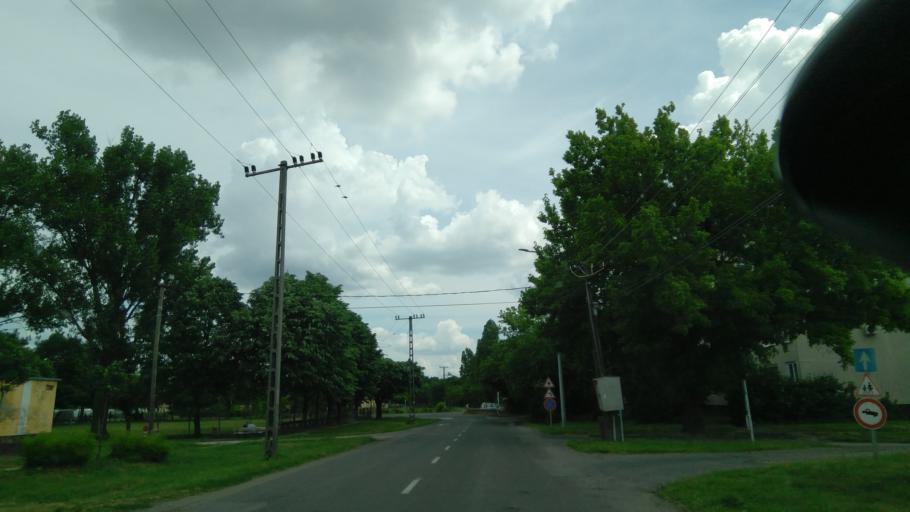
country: HU
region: Bekes
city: Mezohegyes
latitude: 46.3181
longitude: 20.8202
